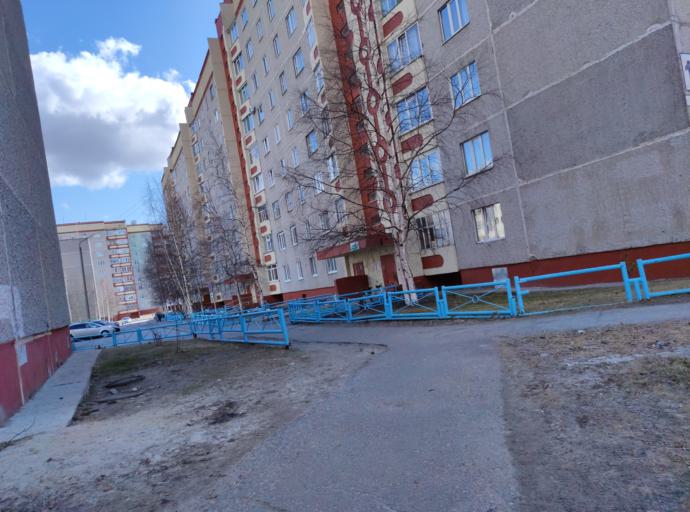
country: RU
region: Khanty-Mansiyskiy Avtonomnyy Okrug
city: Langepas
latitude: 61.2510
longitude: 75.1825
